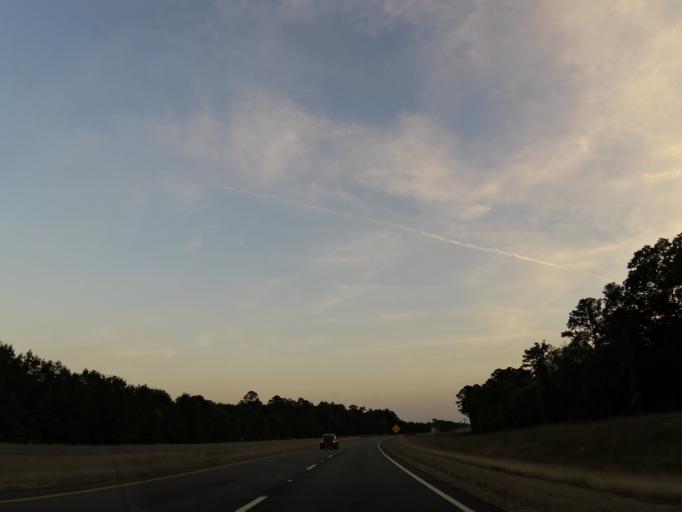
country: US
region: Mississippi
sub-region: Kemper County
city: De Kalb
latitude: 32.8051
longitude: -88.4546
